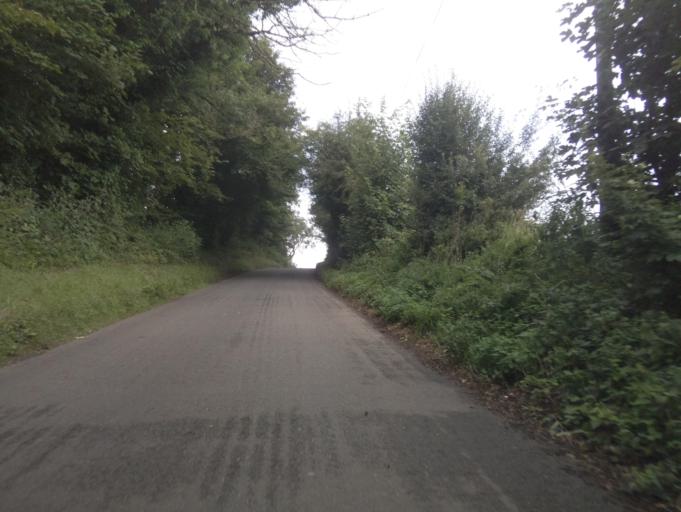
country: GB
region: England
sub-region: Somerset
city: Evercreech
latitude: 51.1740
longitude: -2.5071
